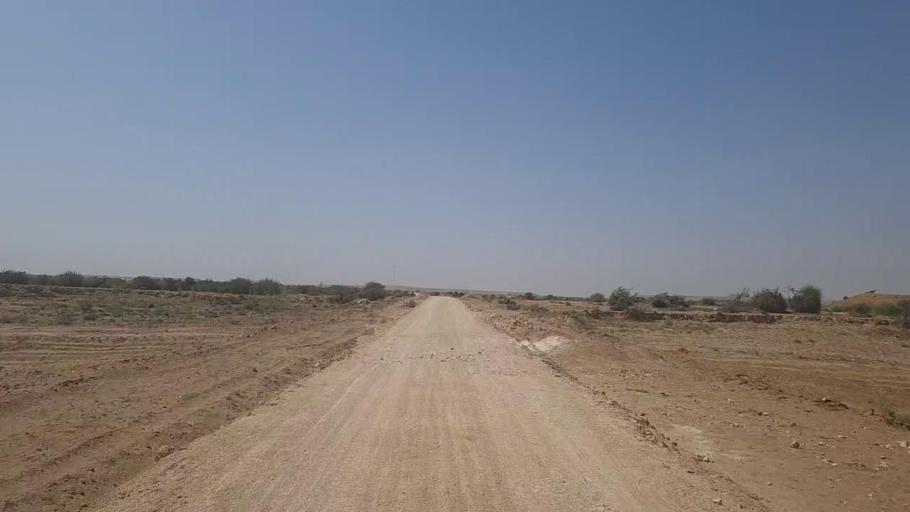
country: PK
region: Sindh
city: Kotri
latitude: 25.1505
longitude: 68.1574
